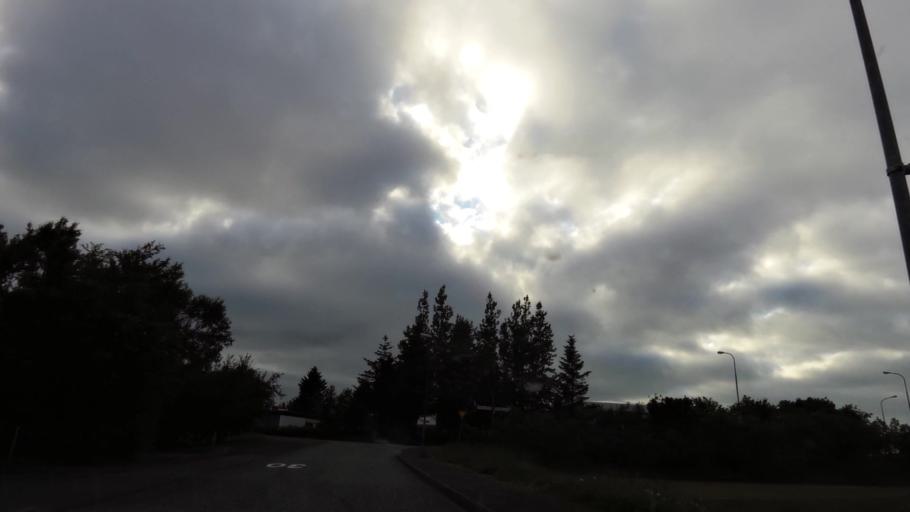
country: IS
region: Capital Region
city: Hafnarfjoerdur
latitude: 64.0700
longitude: -21.9407
